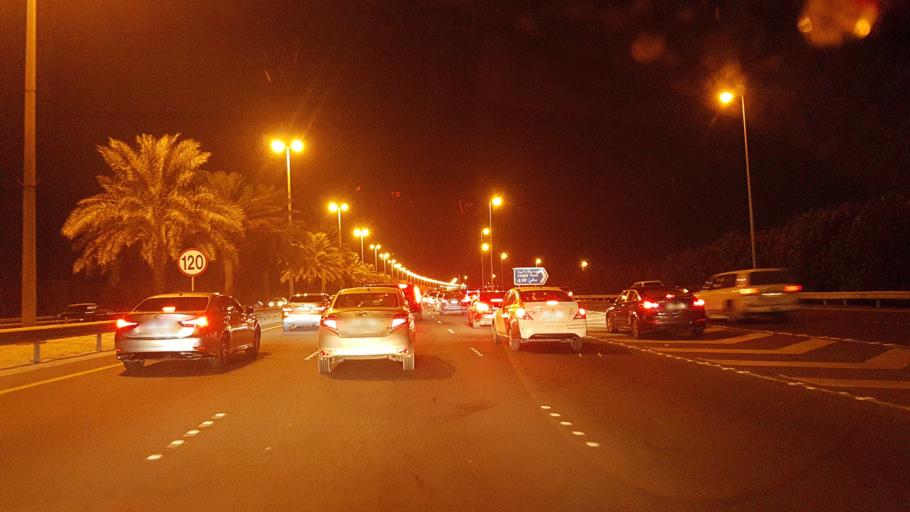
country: BH
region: Northern
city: Madinat `Isa
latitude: 26.1614
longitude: 50.5046
